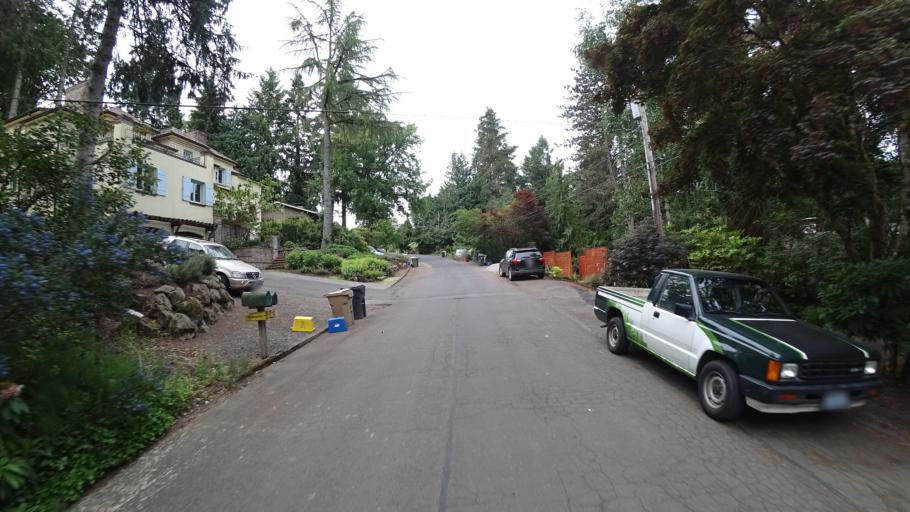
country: US
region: Oregon
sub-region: Clackamas County
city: Lake Oswego
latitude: 45.4278
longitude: -122.6759
